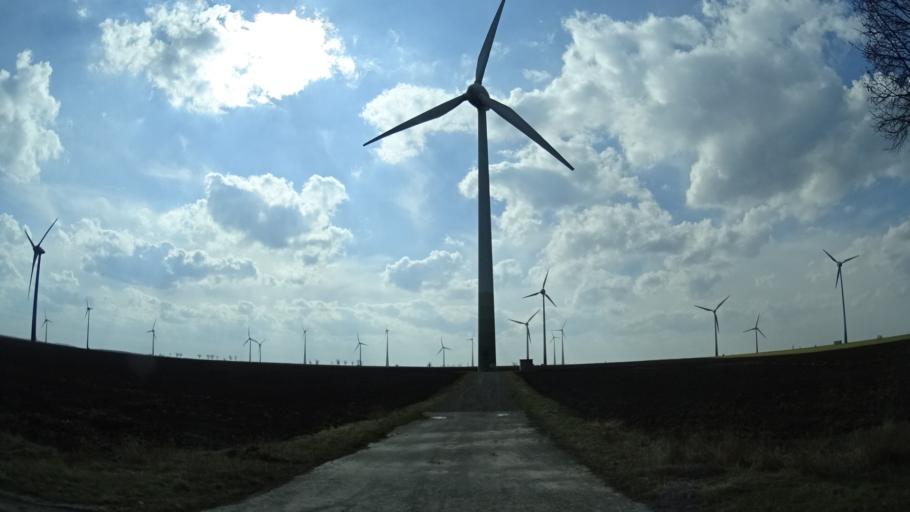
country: DE
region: Saxony-Anhalt
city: Stossen
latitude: 51.1050
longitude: 11.9349
